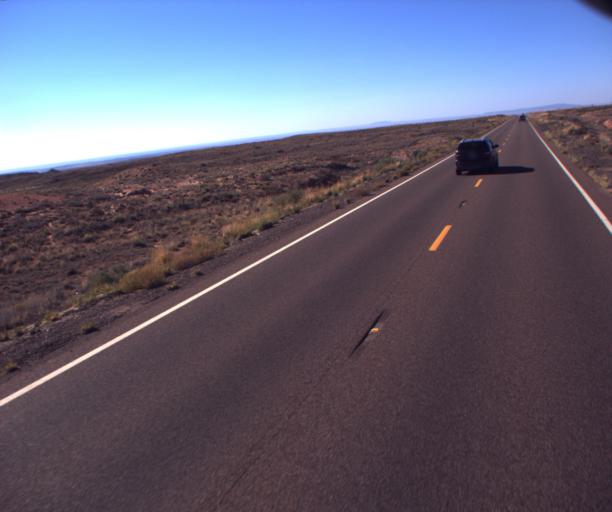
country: US
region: Arizona
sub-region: Navajo County
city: Winslow
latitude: 35.1342
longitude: -110.4921
